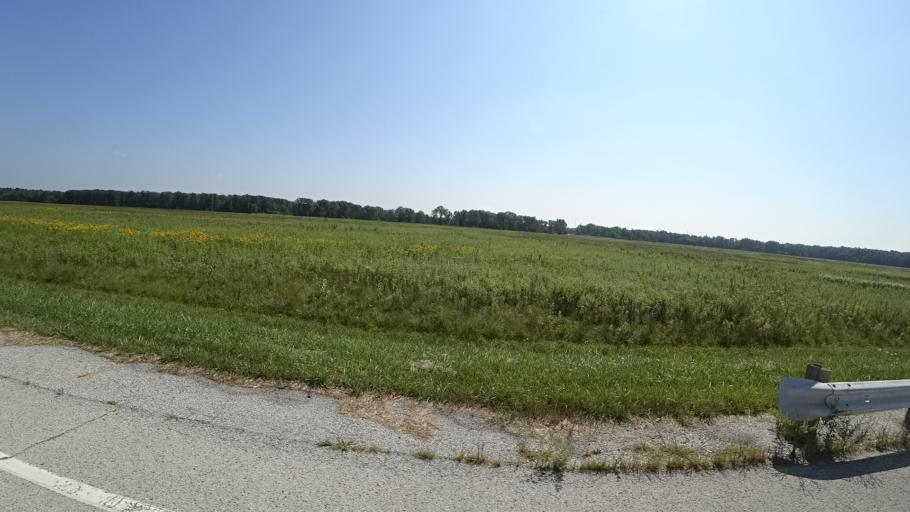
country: US
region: Illinois
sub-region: Cook County
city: Country Club Hills
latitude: 41.5438
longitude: -87.7519
